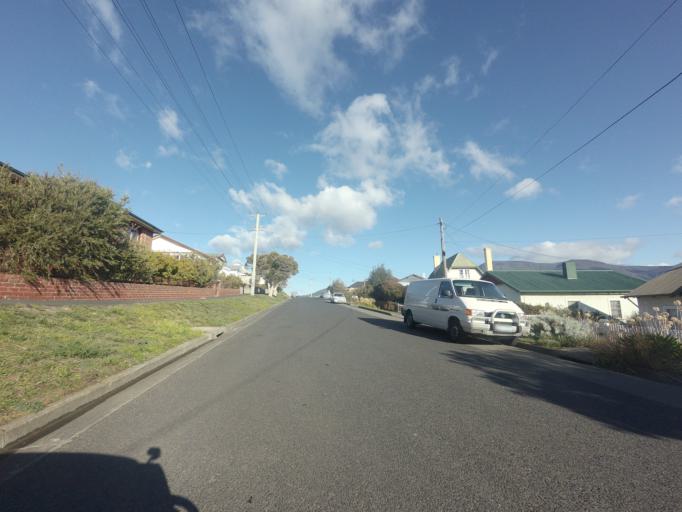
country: AU
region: Tasmania
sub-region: Glenorchy
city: Lutana
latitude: -42.8369
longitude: 147.3076
